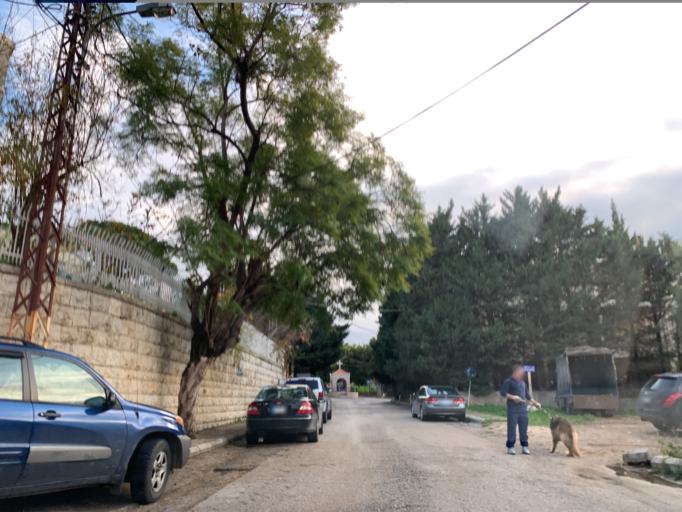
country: LB
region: Mont-Liban
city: Baabda
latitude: 33.8527
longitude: 35.5780
